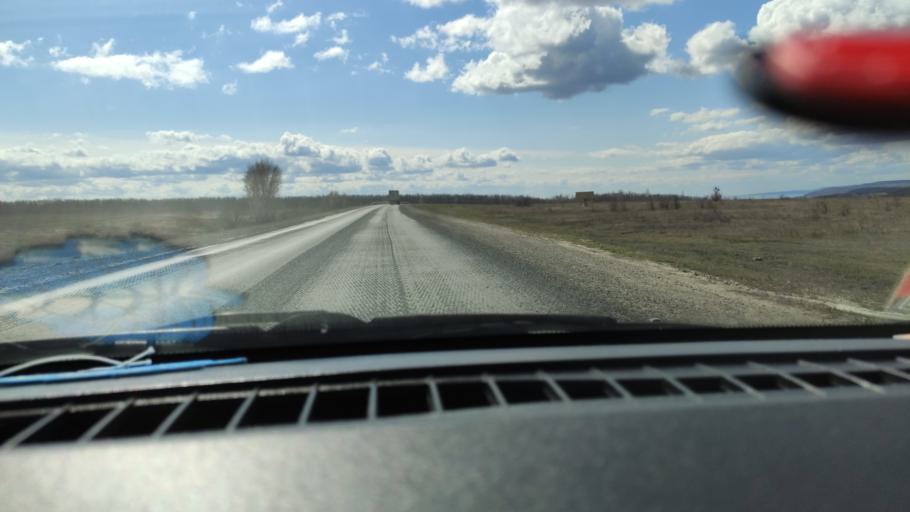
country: RU
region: Saratov
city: Dukhovnitskoye
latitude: 52.7117
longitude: 48.2662
